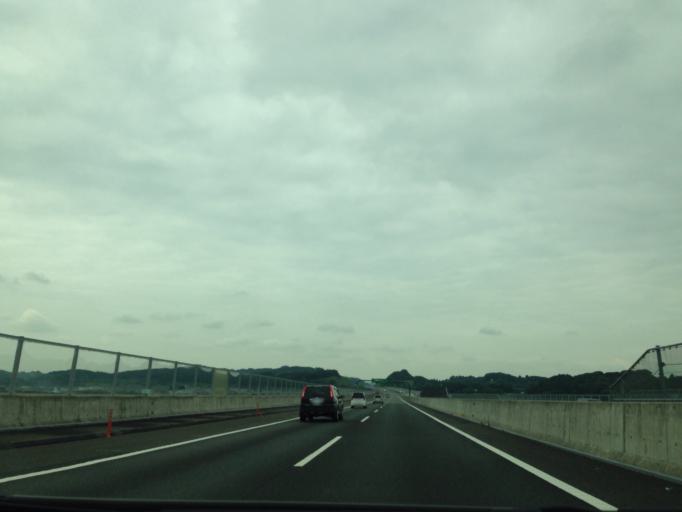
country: JP
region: Shizuoka
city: Mori
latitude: 34.8344
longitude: 137.9708
